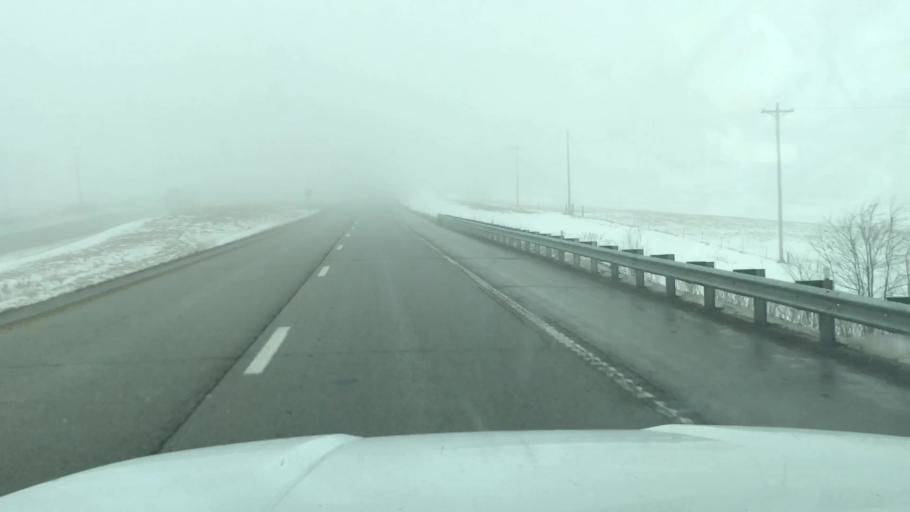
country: US
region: Missouri
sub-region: Clinton County
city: Cameron
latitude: 39.7548
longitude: -94.2958
